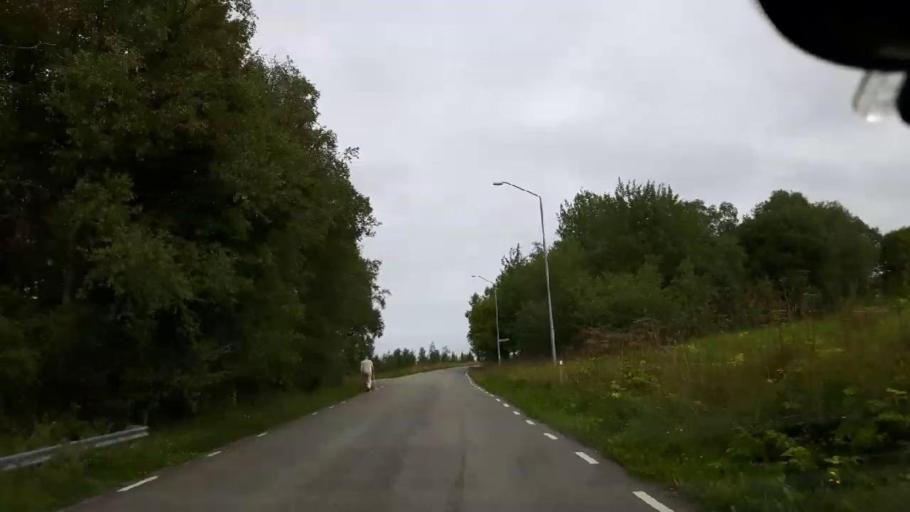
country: SE
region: Jaemtland
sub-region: OEstersunds Kommun
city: Ostersund
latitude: 63.1759
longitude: 14.5166
